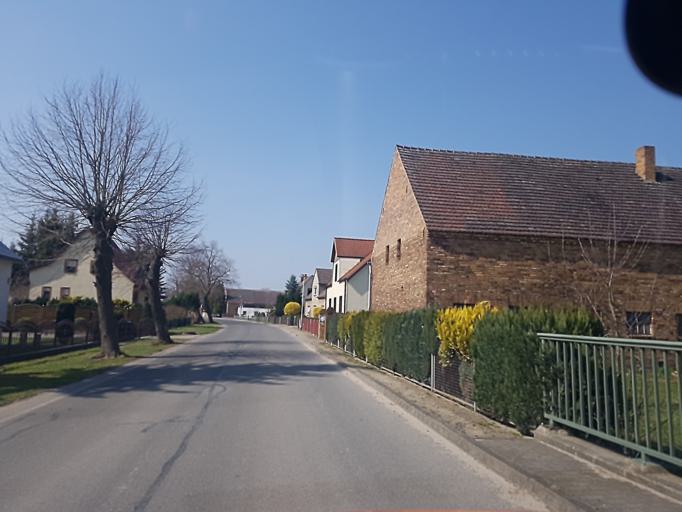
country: DE
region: Brandenburg
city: Forst
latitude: 51.6812
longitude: 14.5603
